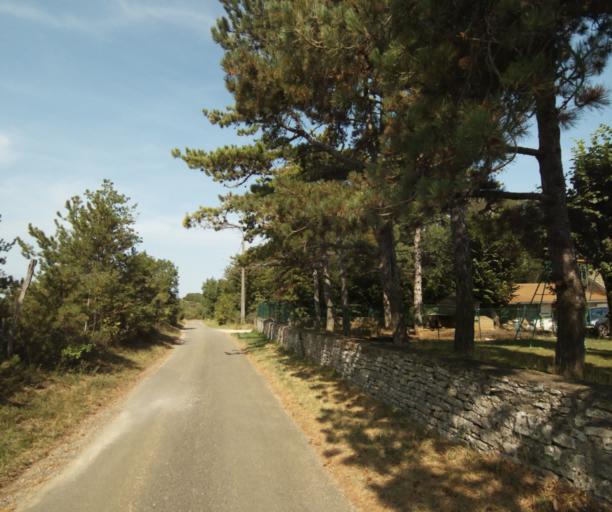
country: FR
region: Bourgogne
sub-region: Departement de Saone-et-Loire
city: Tournus
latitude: 46.5590
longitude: 4.8737
